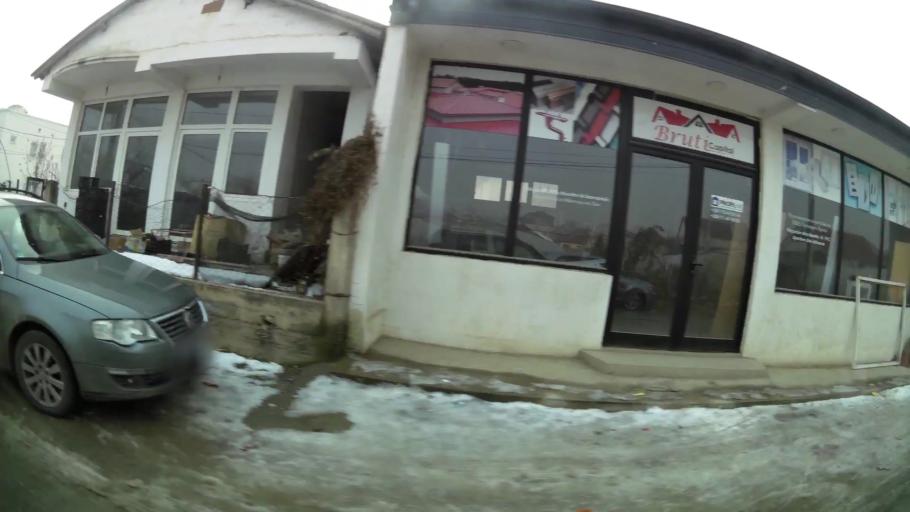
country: MK
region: Suto Orizari
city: Suto Orizare
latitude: 42.0360
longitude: 21.4213
